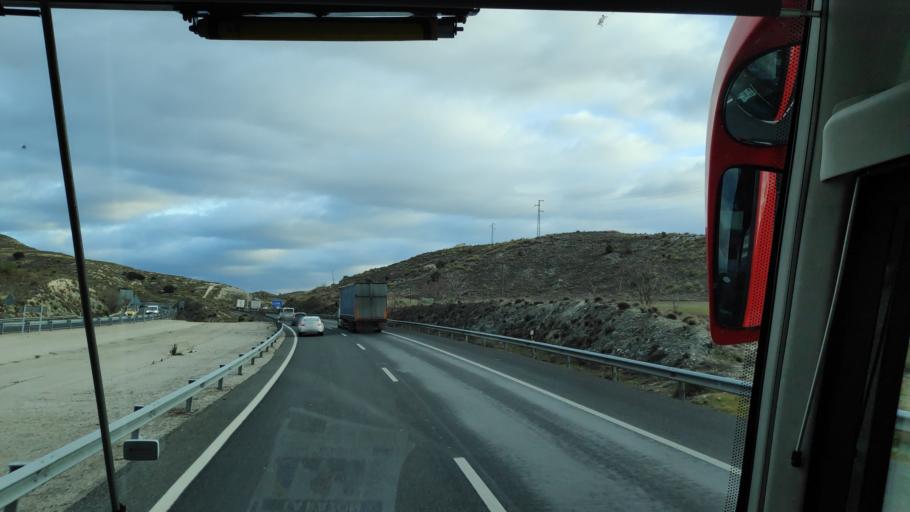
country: ES
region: Madrid
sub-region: Provincia de Madrid
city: Perales de Tajuna
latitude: 40.2149
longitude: -3.3287
